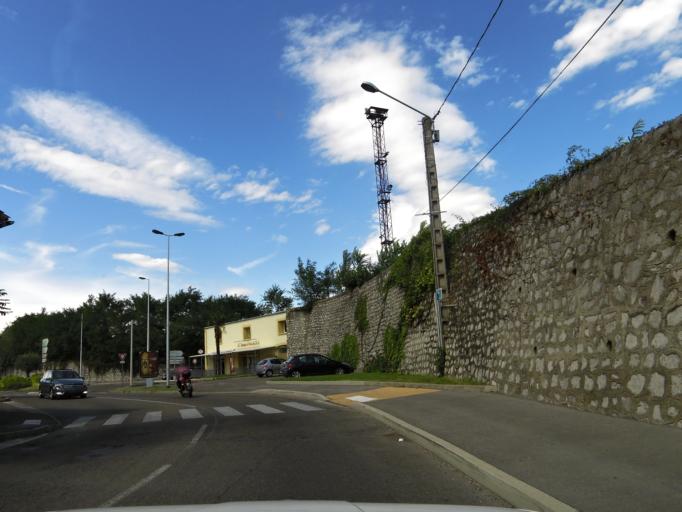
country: FR
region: Languedoc-Roussillon
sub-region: Departement du Gard
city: Ales
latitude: 44.1249
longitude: 4.0918
